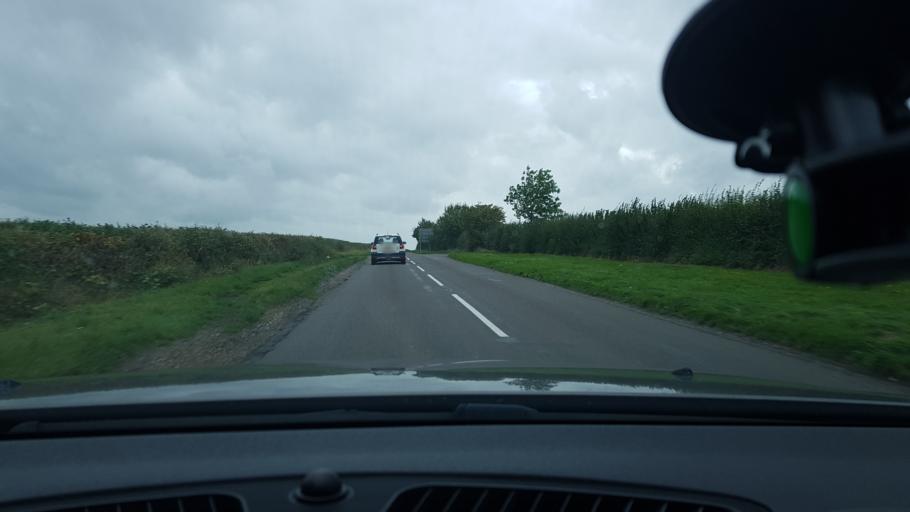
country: GB
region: England
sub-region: Wiltshire
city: Shalbourne
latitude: 51.3516
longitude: -1.5816
